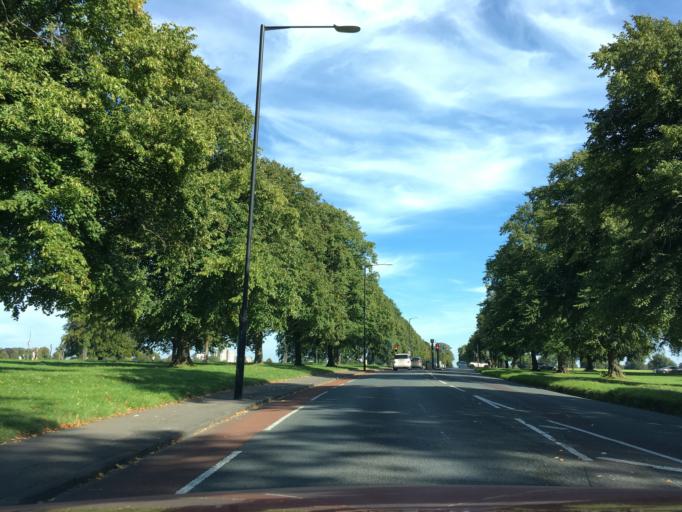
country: GB
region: England
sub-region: Bristol
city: Bristol
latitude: 51.4750
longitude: -2.6258
